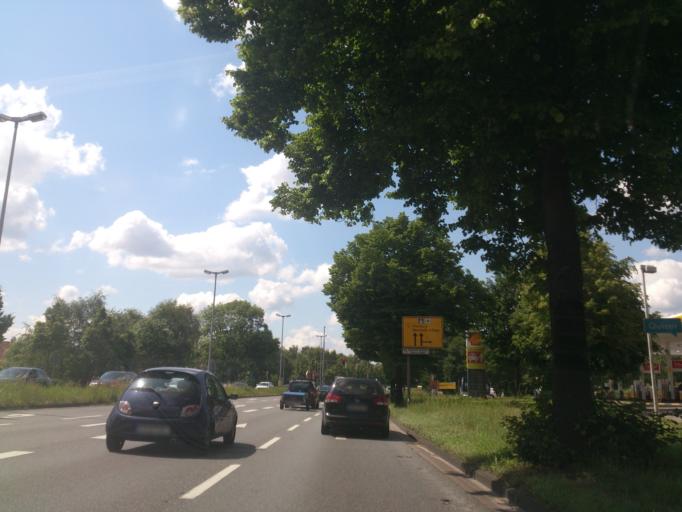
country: DE
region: Lower Saxony
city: Auf der Horst
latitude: 52.4143
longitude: 9.6444
